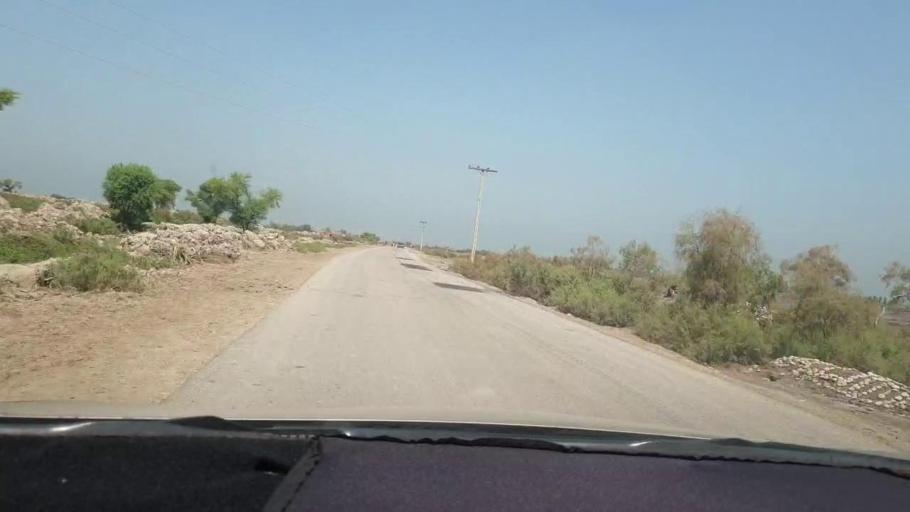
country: PK
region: Sindh
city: Miro Khan
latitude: 27.8228
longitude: 68.0215
